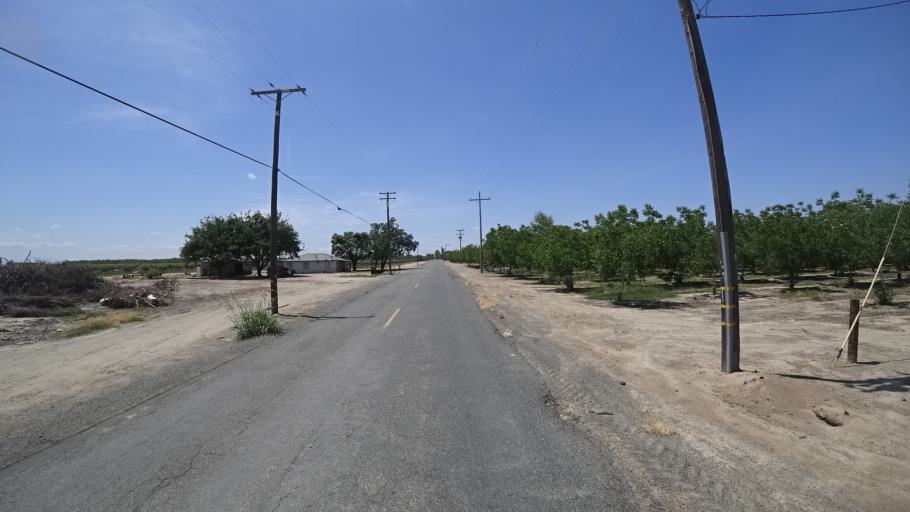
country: US
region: California
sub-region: Kings County
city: Armona
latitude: 36.2837
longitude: -119.6966
